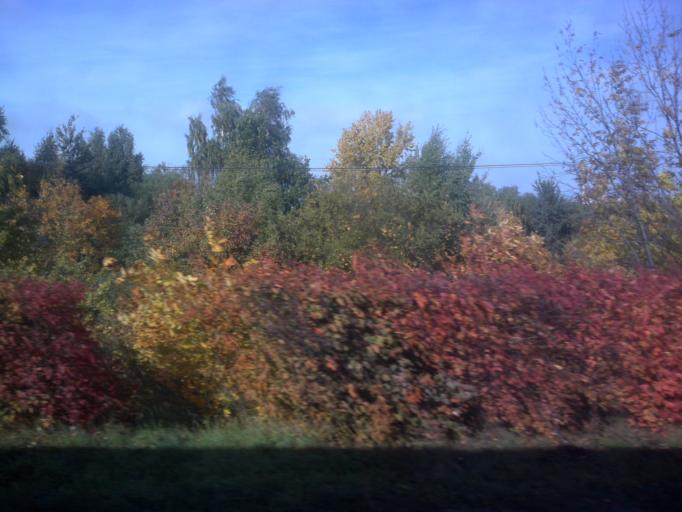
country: RU
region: Moskovskaya
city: Biryulevo Zapadnoye
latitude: 55.6083
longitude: 37.6372
